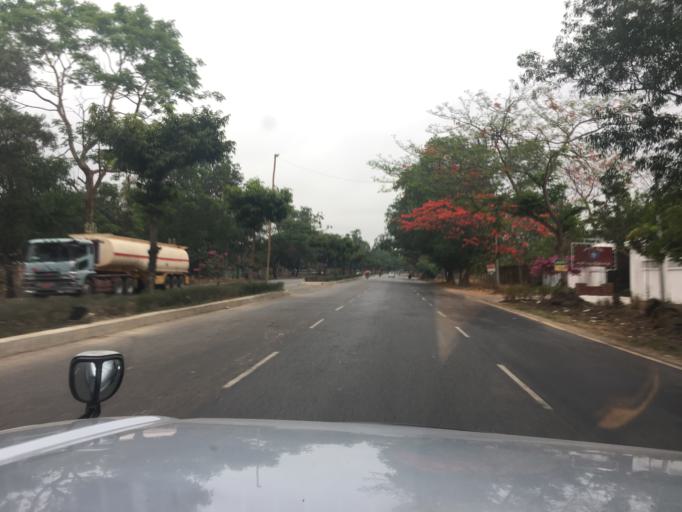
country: MM
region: Bago
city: Thanatpin
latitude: 17.1943
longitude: 96.3998
